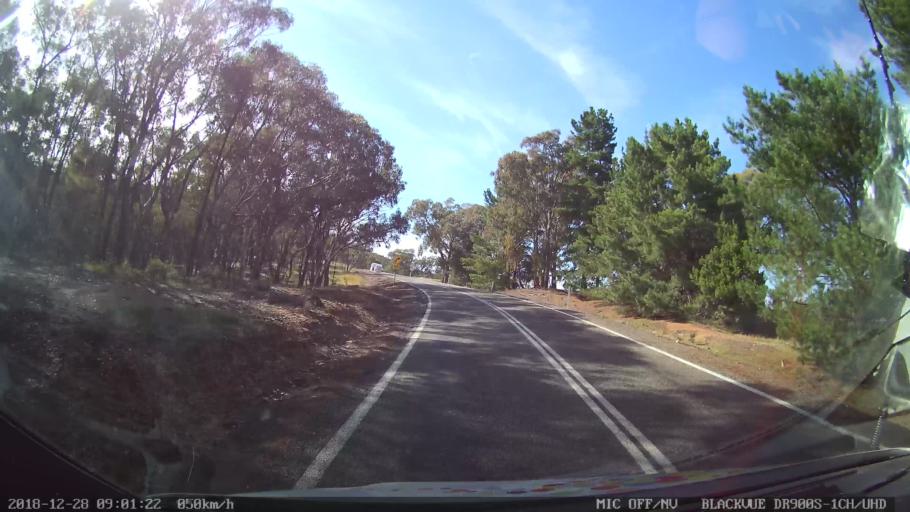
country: AU
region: New South Wales
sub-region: Upper Lachlan Shire
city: Crookwell
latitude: -34.1459
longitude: 149.3333
